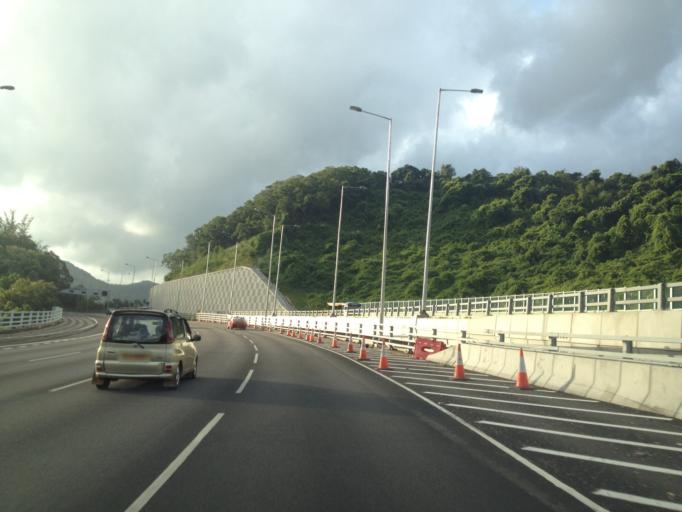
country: HK
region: Tai Po
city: Tai Po
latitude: 22.4471
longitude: 114.1549
